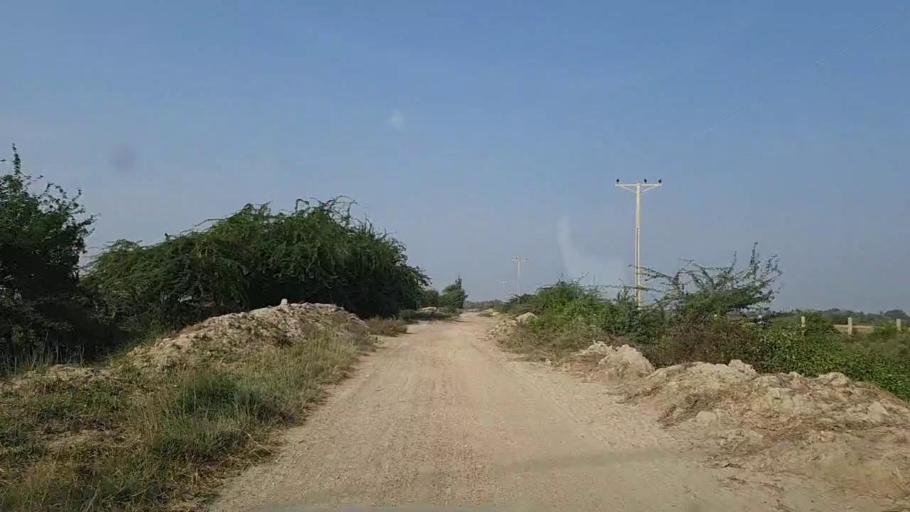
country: PK
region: Sindh
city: Mirpur Sakro
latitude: 24.5813
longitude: 67.5678
